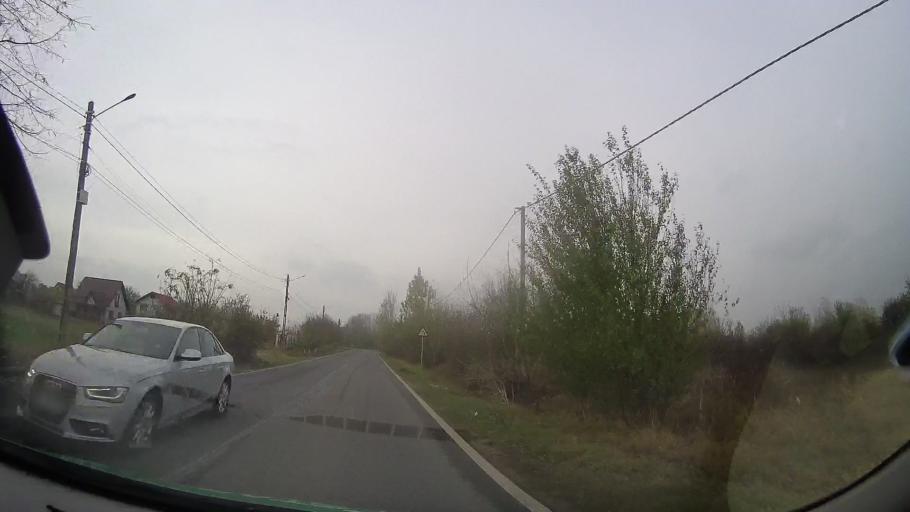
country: RO
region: Ilfov
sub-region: Comuna Gruiu
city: Silistea Snagovului
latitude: 44.7497
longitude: 26.1957
